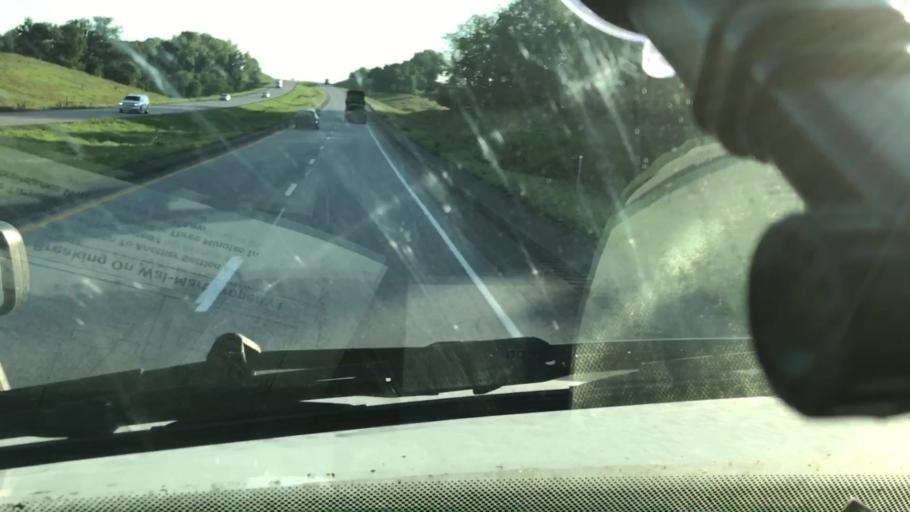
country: US
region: Iowa
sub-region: Pottawattamie County
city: Council Bluffs
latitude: 41.3306
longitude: -95.7424
